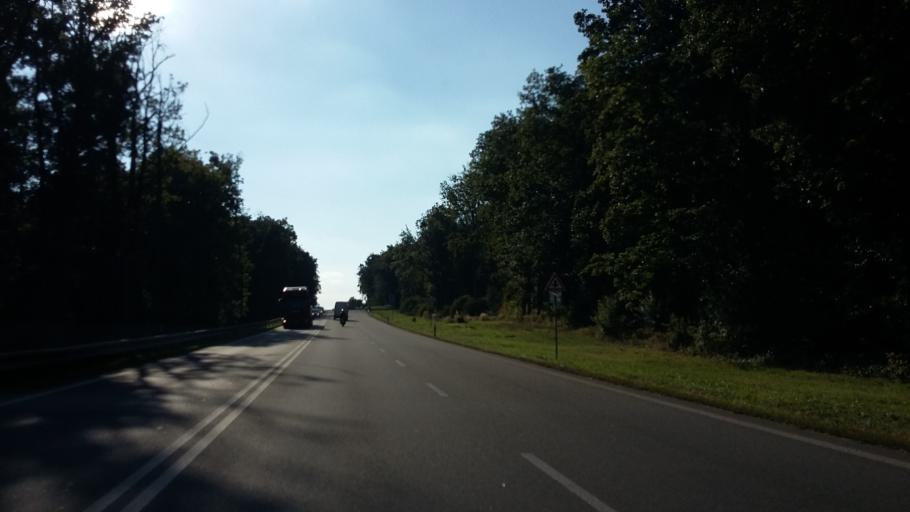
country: CZ
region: South Moravian
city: Troubsko
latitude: 49.1897
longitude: 16.4600
